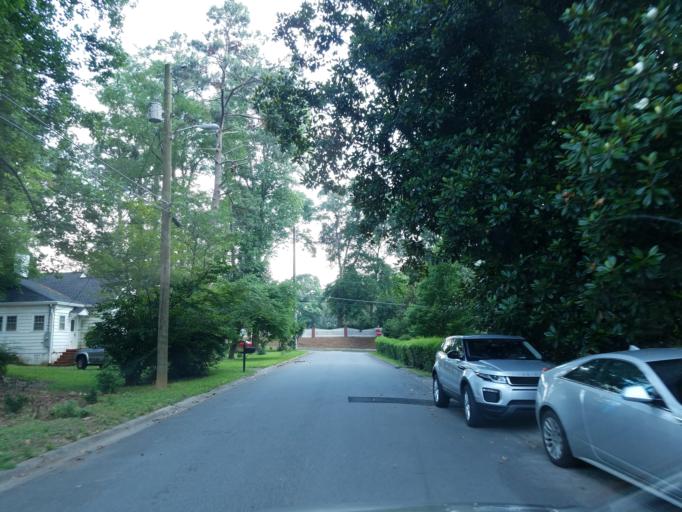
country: US
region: Georgia
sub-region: Cobb County
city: Marietta
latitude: 33.9526
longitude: -84.5618
